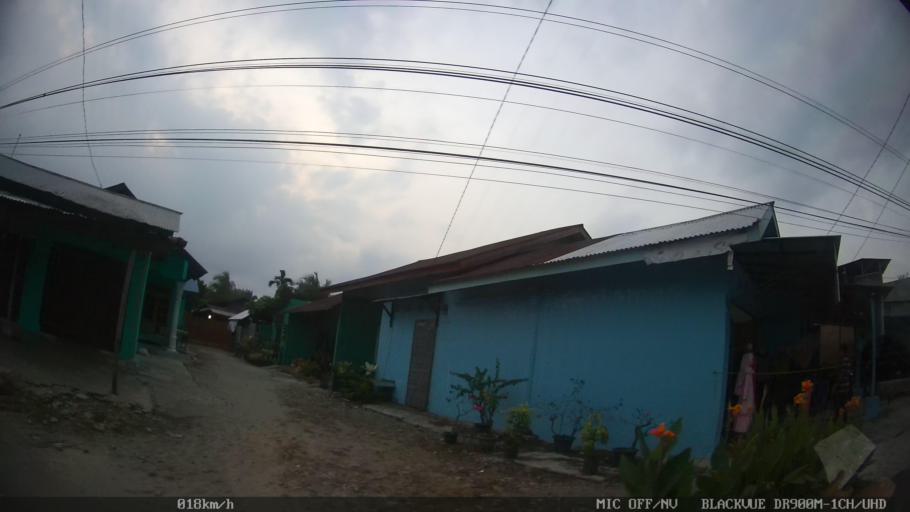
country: ID
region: North Sumatra
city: Sunggal
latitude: 3.5686
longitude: 98.5810
